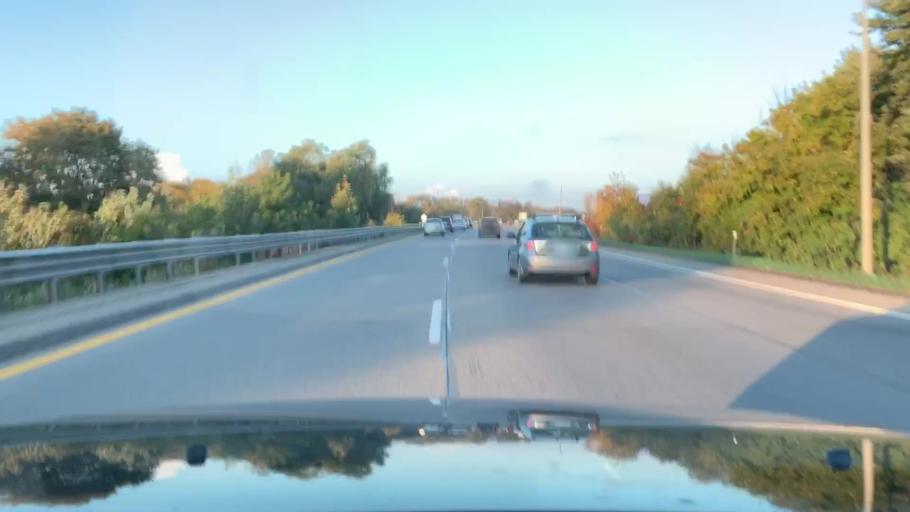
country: US
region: Michigan
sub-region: Kent County
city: Grandville
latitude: 42.9194
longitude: -85.7601
